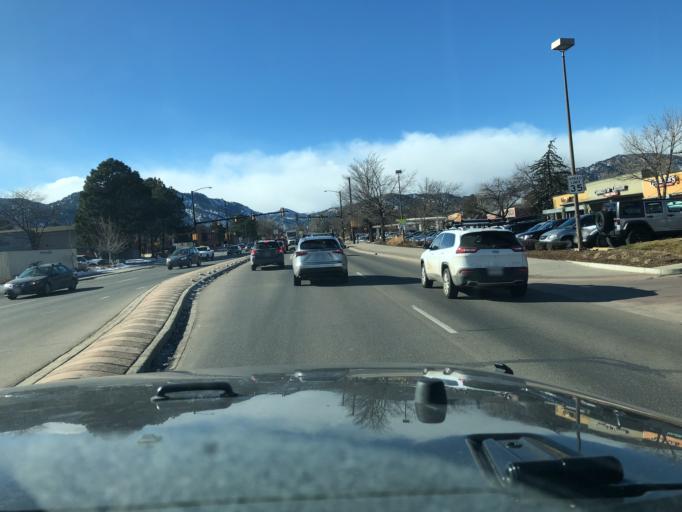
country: US
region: Colorado
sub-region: Boulder County
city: Boulder
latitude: 40.0147
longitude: -105.2593
